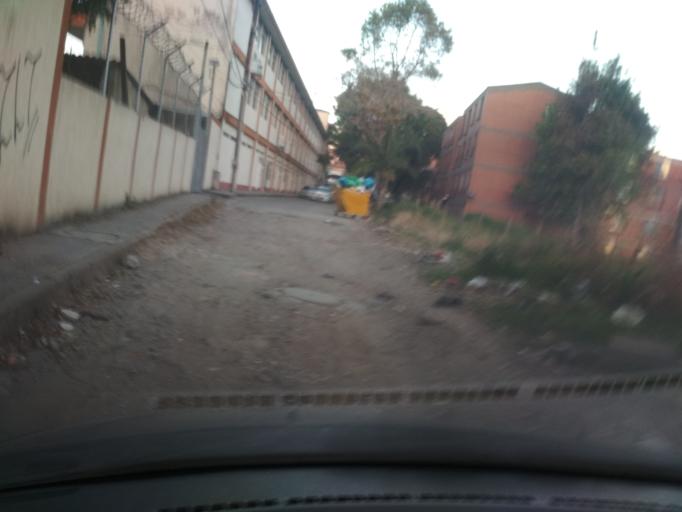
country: CO
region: Cauca
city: Popayan
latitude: 2.4498
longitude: -76.6072
